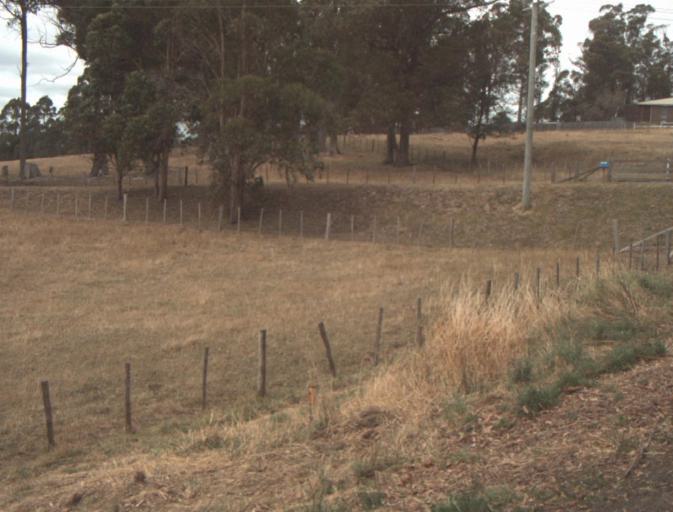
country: AU
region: Tasmania
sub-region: Launceston
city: Mayfield
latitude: -41.2007
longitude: 147.2176
